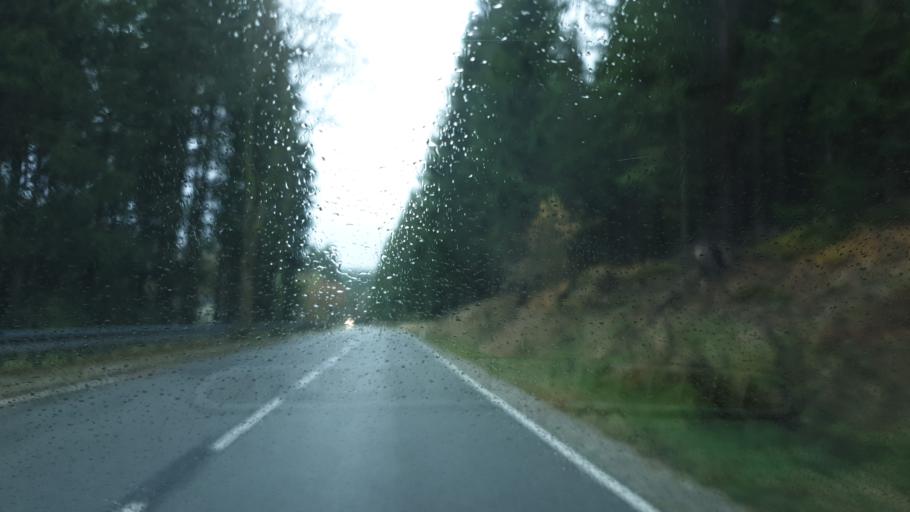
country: DE
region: Saxony
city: Muldenhammer
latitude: 50.4697
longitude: 12.5000
